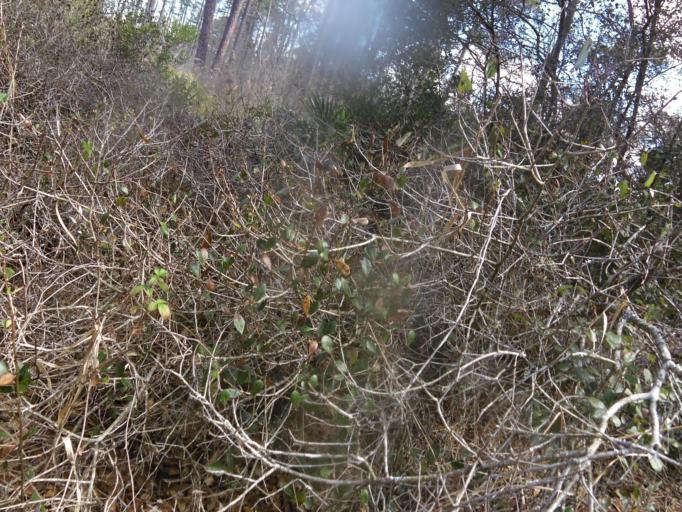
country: US
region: Florida
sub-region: Putnam County
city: Interlachen
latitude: 29.7629
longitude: -81.8509
